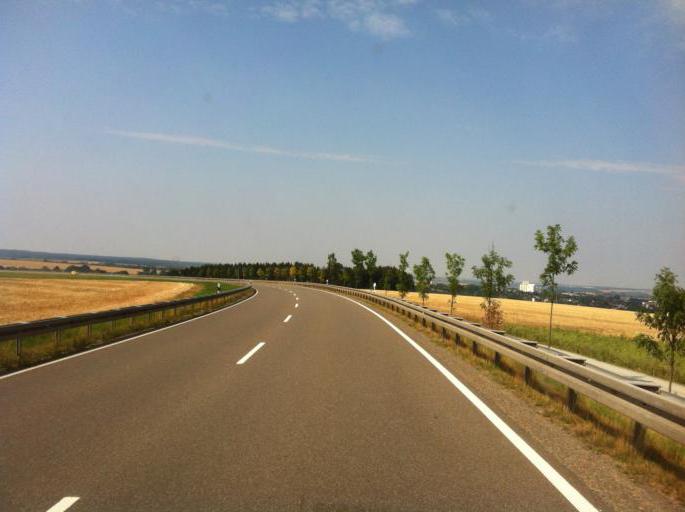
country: DE
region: Saxony
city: Neumark
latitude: 50.6307
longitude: 12.3431
